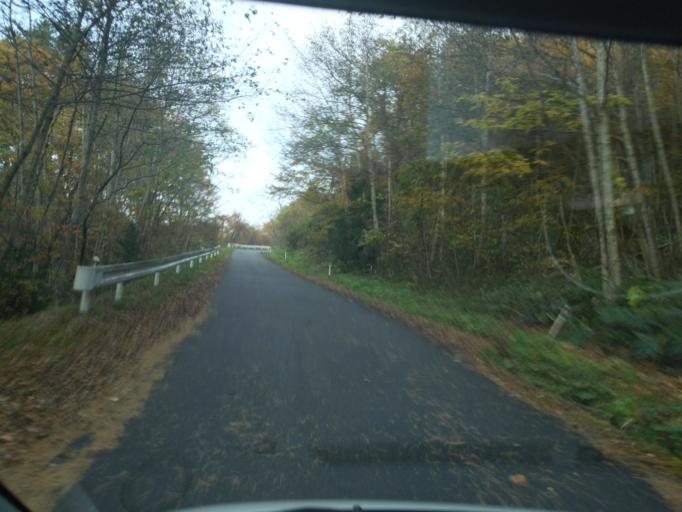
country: JP
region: Iwate
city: Ichinoseki
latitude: 38.9927
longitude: 141.0078
